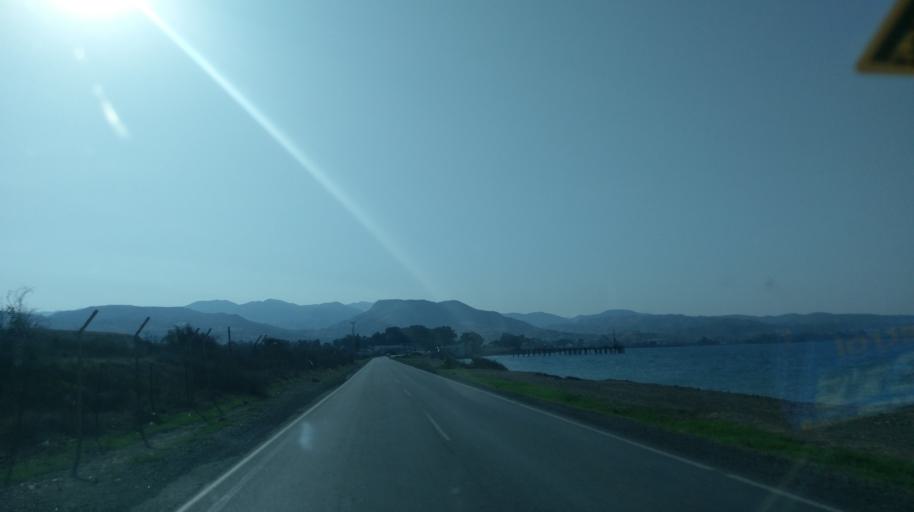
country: CY
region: Lefkosia
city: Lefka
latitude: 35.1448
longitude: 32.8427
